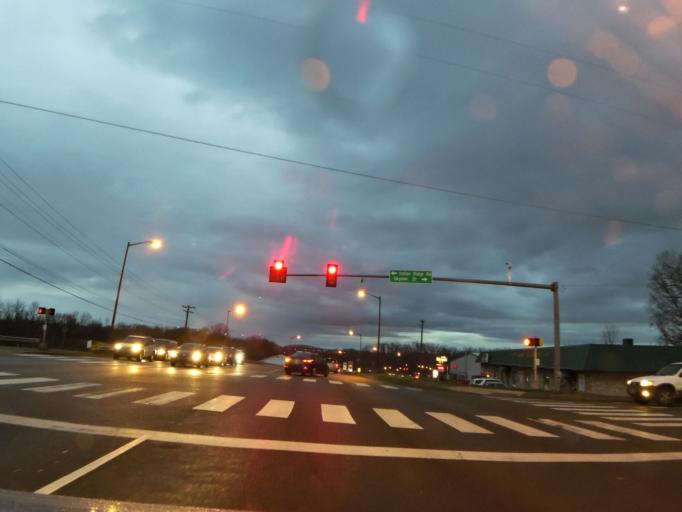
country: US
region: Tennessee
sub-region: Washington County
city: Midway
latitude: 36.3208
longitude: -82.3944
